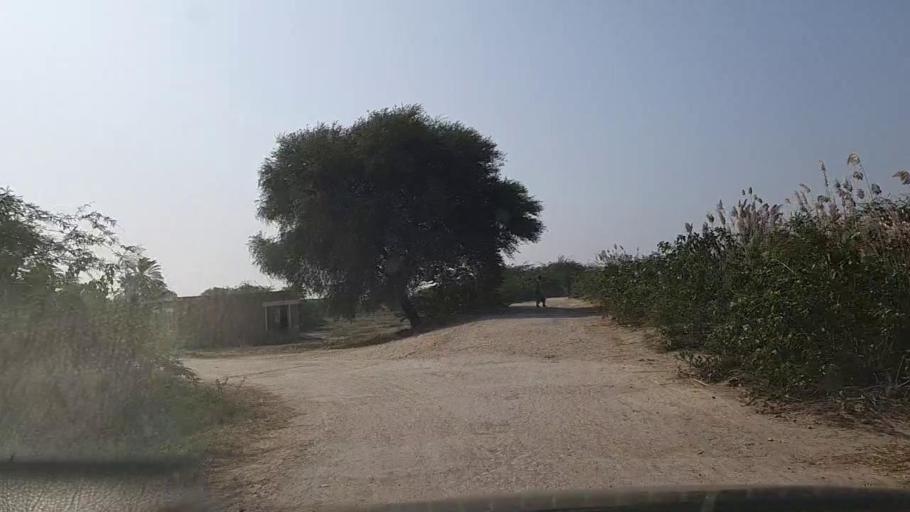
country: PK
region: Sindh
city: Gharo
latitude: 24.7050
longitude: 67.6470
